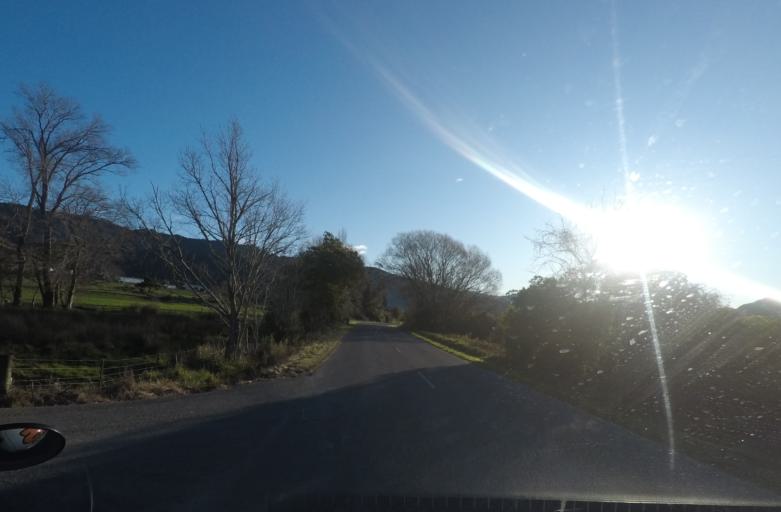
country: NZ
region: Marlborough
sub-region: Marlborough District
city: Picton
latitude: -41.2930
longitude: 173.8338
